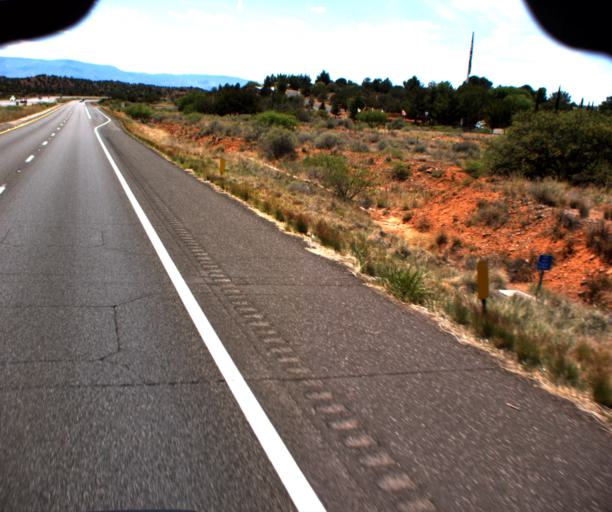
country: US
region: Arizona
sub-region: Yavapai County
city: West Sedona
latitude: 34.8425
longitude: -111.8639
